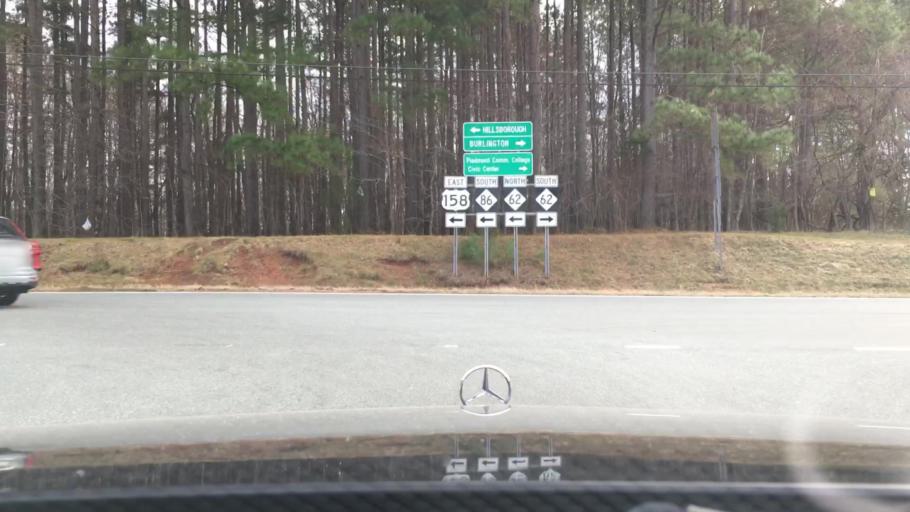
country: US
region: North Carolina
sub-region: Caswell County
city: Yanceyville
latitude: 36.4055
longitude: -79.3218
